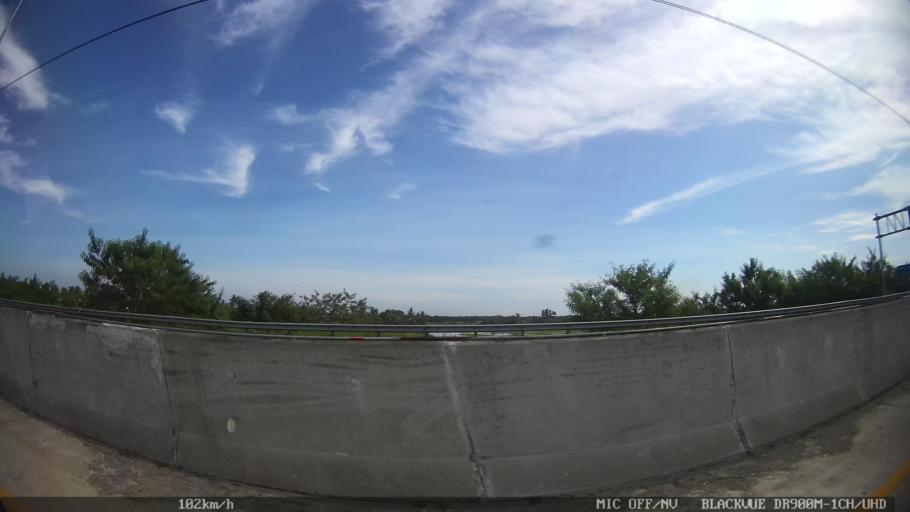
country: ID
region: North Sumatra
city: Sunggal
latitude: 3.6429
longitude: 98.5635
